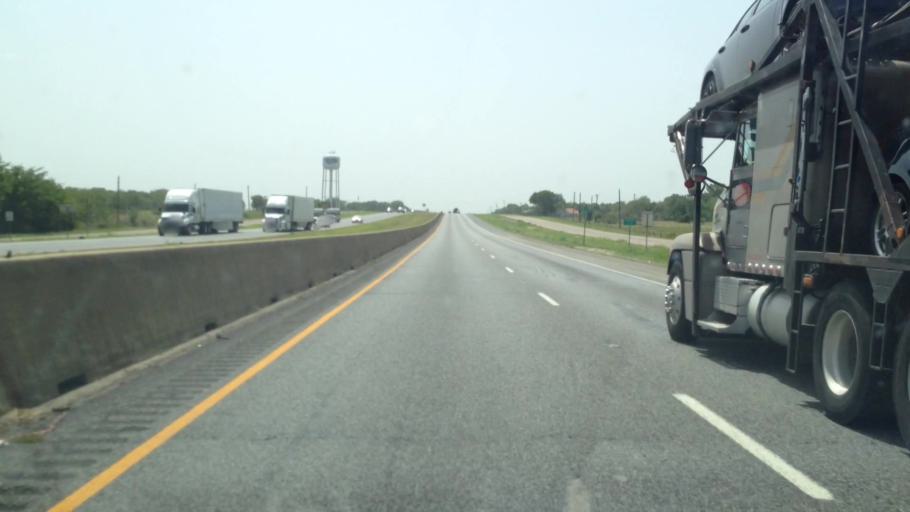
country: US
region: Texas
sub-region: Hunt County
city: Commerce
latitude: 33.1299
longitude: -95.8792
